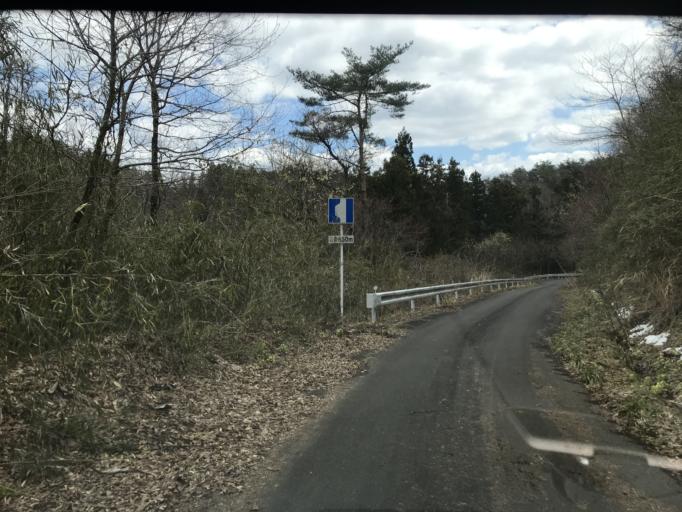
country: JP
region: Iwate
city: Ichinoseki
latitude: 38.9508
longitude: 141.0891
